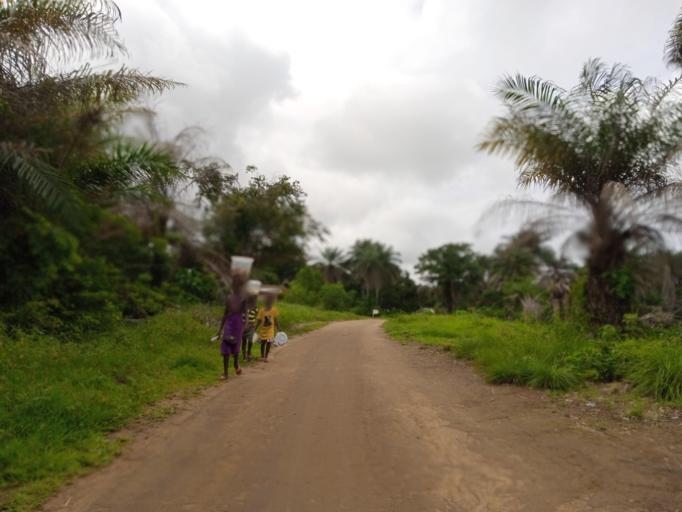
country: SL
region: Northern Province
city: Masoyila
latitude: 8.5815
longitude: -13.1903
